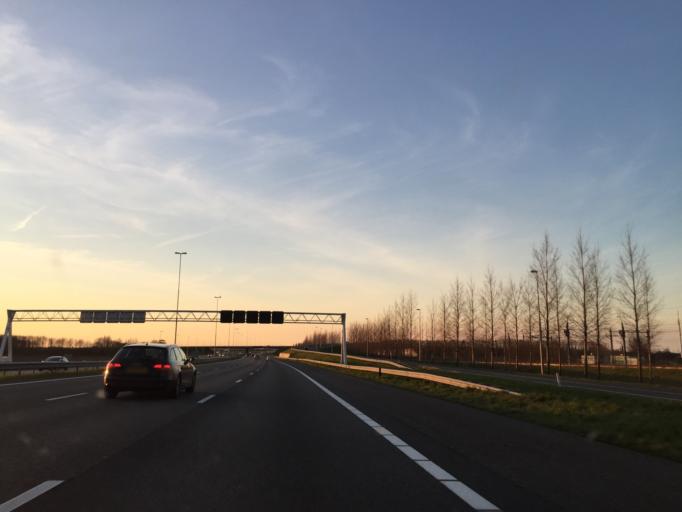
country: NL
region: North Brabant
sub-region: Gemeente Breda
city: Breda
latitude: 51.6409
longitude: 4.6958
